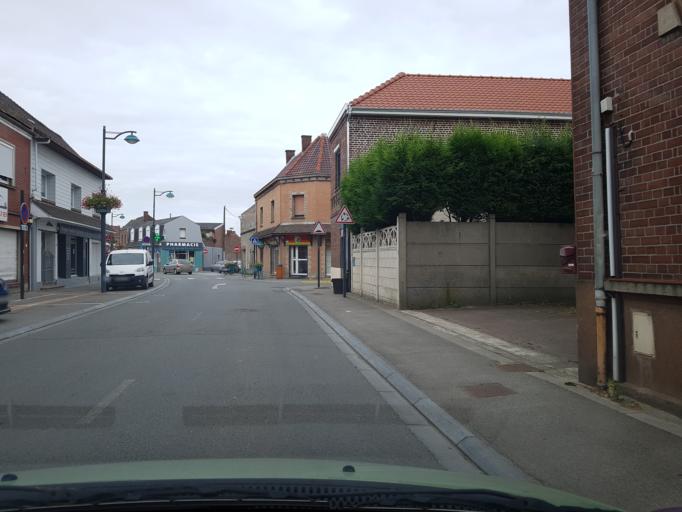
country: FR
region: Nord-Pas-de-Calais
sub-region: Departement du Pas-de-Calais
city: Billy-Berclau
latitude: 50.5225
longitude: 2.8729
